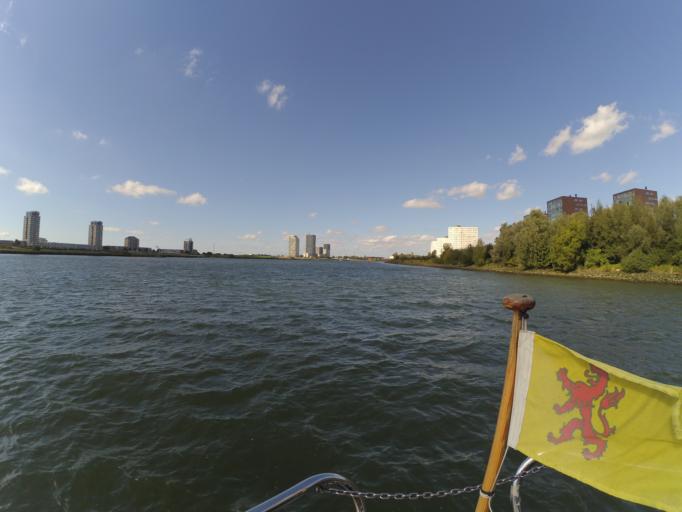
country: NL
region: South Holland
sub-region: Gemeente Spijkenisse
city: Spijkenisse
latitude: 51.8479
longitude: 4.3597
